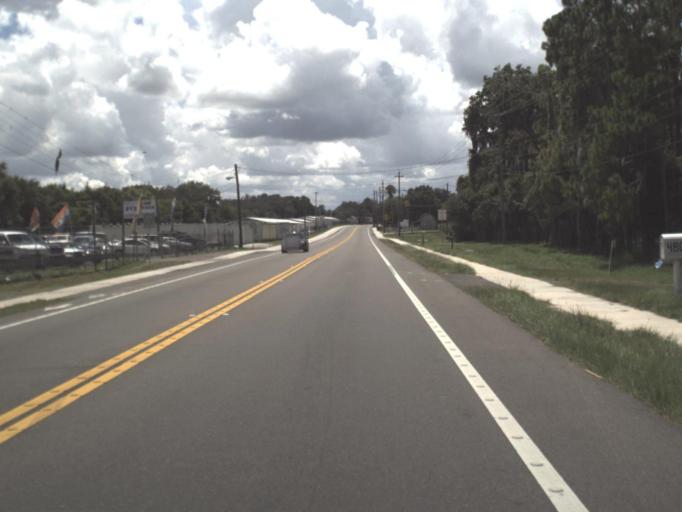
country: US
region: Florida
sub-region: Hillsborough County
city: Dover
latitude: 28.0054
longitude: -82.1767
